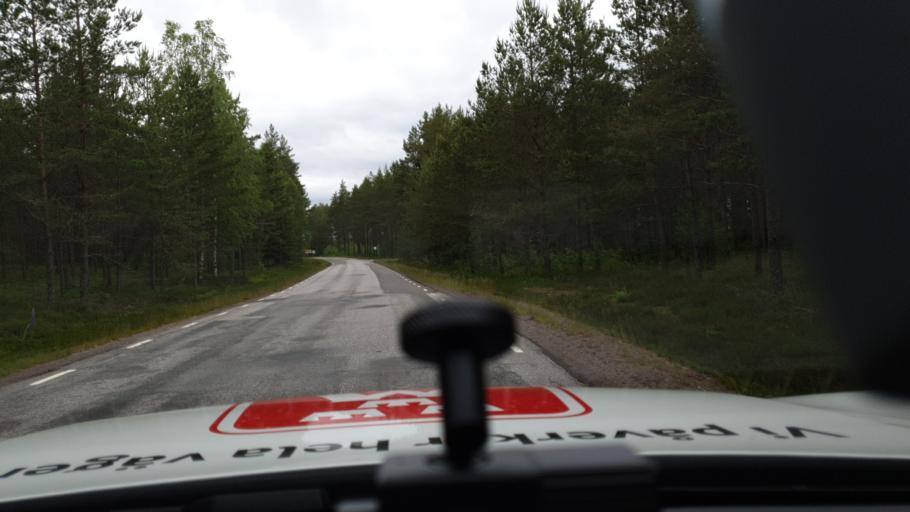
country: SE
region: Vaestra Goetaland
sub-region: Toreboda Kommun
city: Toereboda
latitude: 58.6991
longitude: 14.1886
